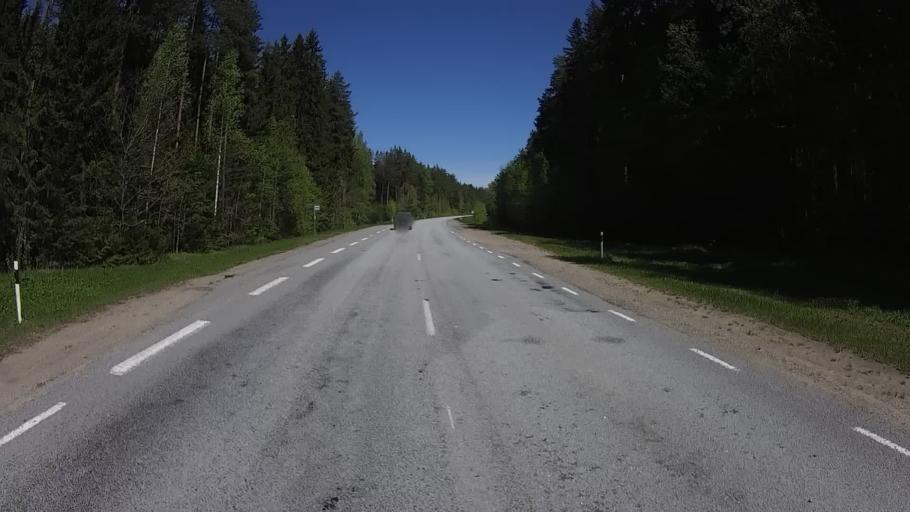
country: EE
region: Polvamaa
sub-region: Raepina vald
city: Rapina
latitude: 58.0558
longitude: 27.3875
